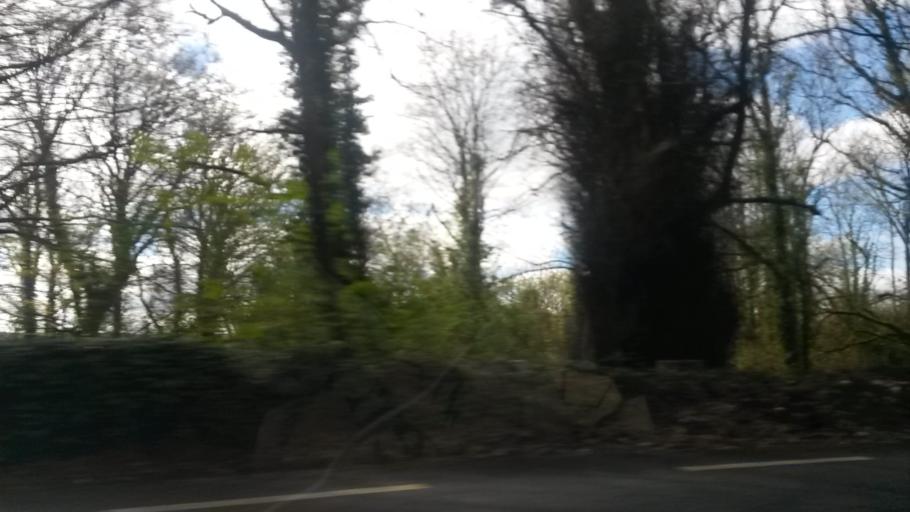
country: IE
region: Munster
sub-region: County Cork
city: Carrigtwohill
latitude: 51.8945
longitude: -8.2828
